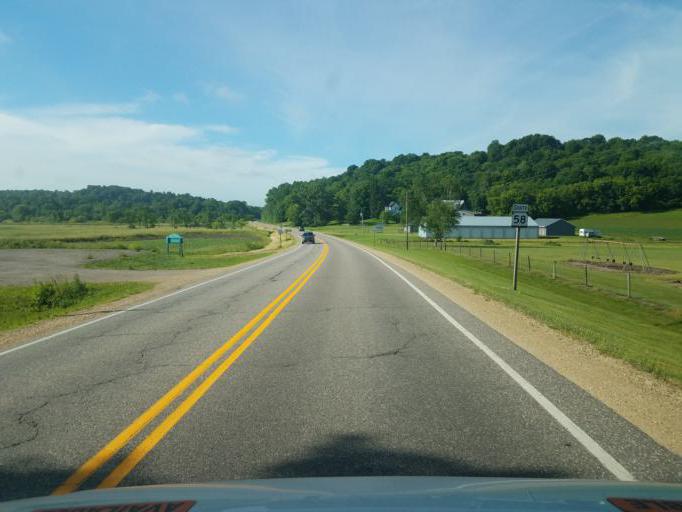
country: US
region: Wisconsin
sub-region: Sauk County
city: Reedsburg
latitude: 43.5779
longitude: -90.1344
